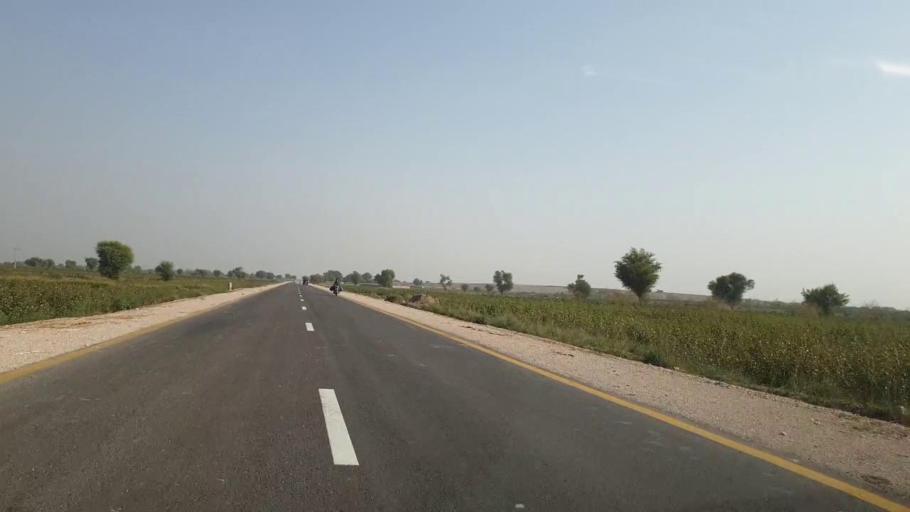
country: PK
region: Sindh
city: Sehwan
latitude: 26.4624
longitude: 67.8009
